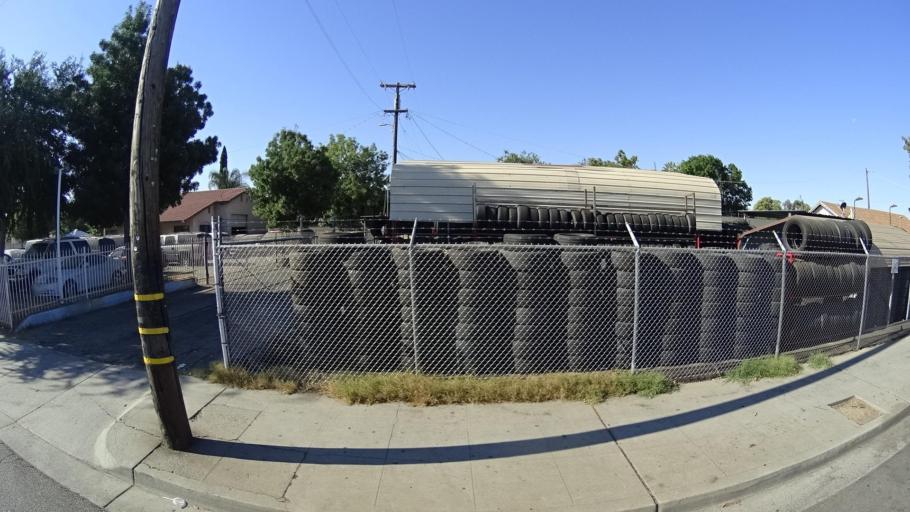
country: US
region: California
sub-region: Fresno County
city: Fresno
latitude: 36.7503
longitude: -119.7879
